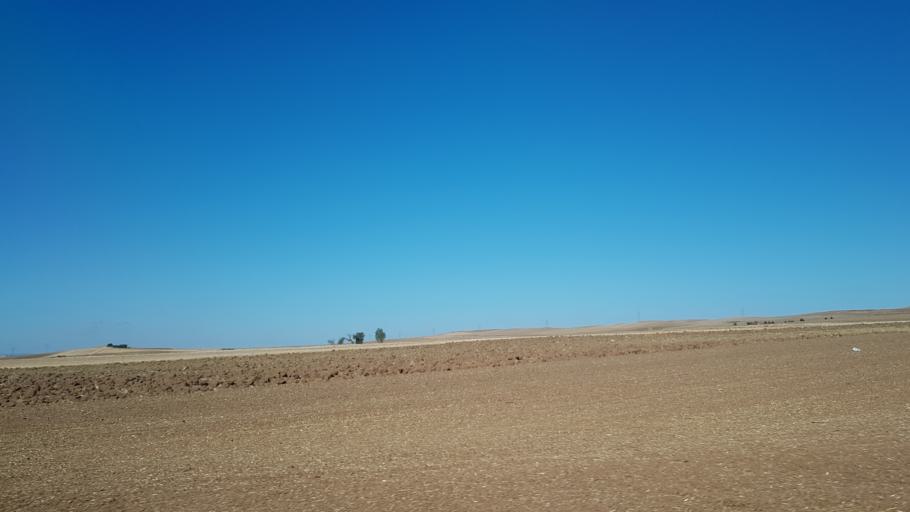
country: TR
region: Tekirdag
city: Corlu
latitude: 41.0155
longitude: 27.8061
